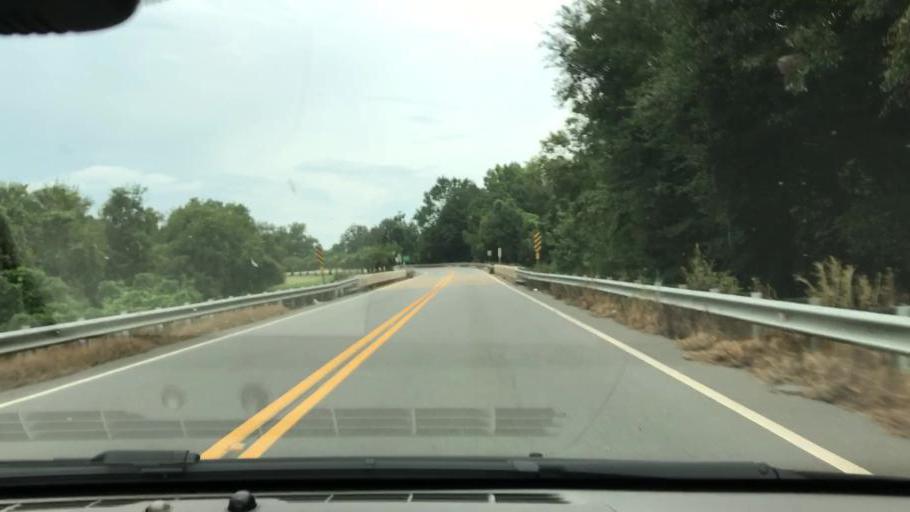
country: US
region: Alabama
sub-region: Houston County
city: Ashford
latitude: 31.2901
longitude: -85.1038
